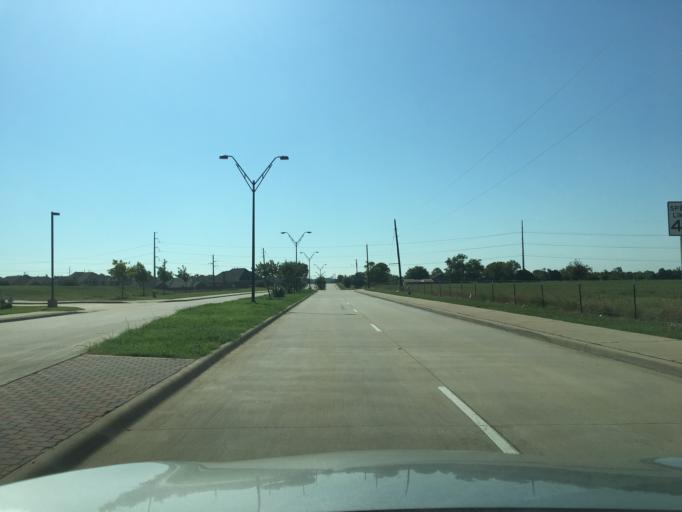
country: US
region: Texas
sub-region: Dallas County
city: Sachse
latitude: 32.9657
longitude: -96.6029
